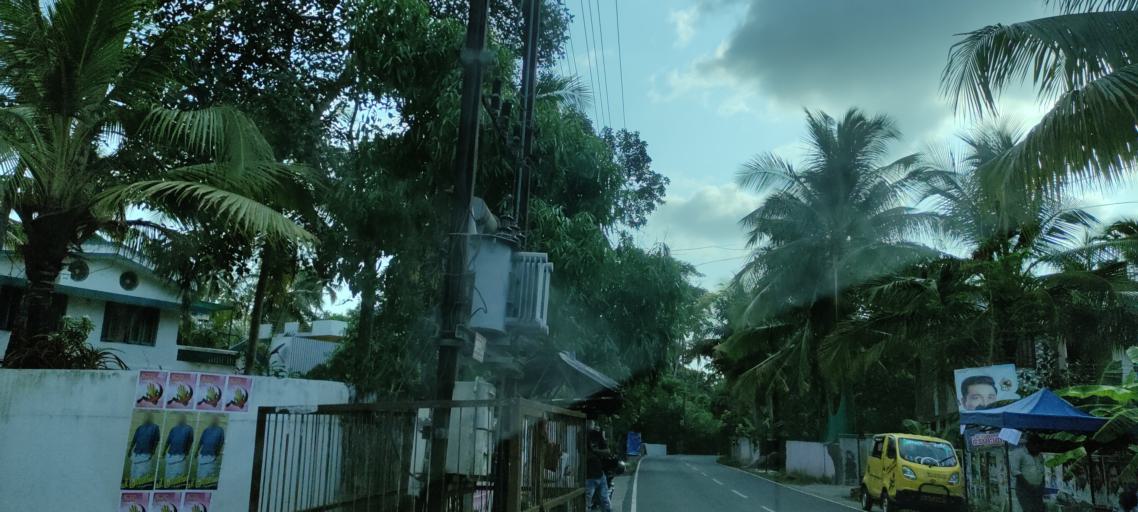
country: IN
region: Kerala
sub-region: Alappuzha
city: Vayalar
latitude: 9.6812
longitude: 76.3257
